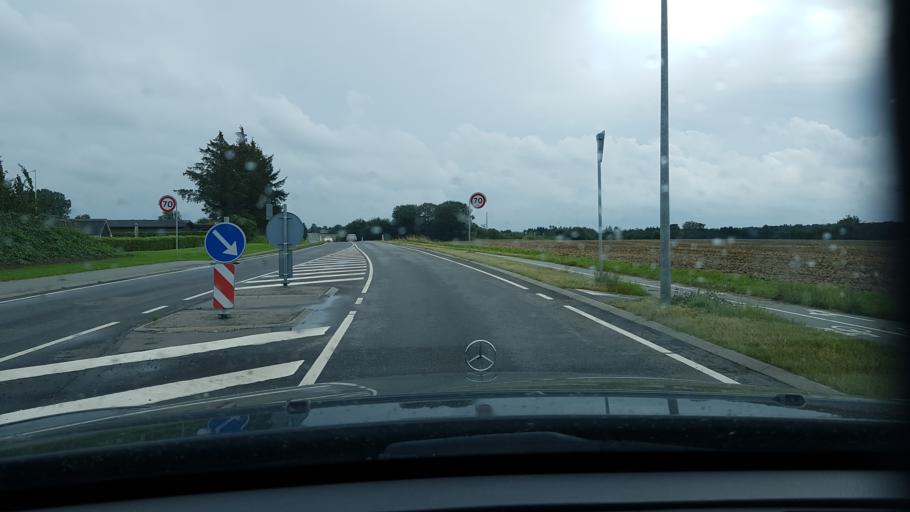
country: DK
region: North Denmark
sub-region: Mariagerfjord Kommune
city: Hadsund
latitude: 56.7680
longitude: 10.2842
